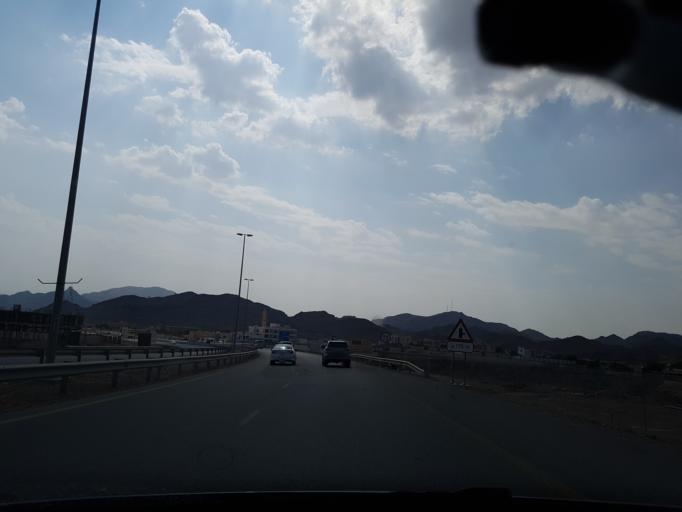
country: AE
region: Al Fujayrah
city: Dibba Al-Fujairah
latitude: 25.5135
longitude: 56.0765
